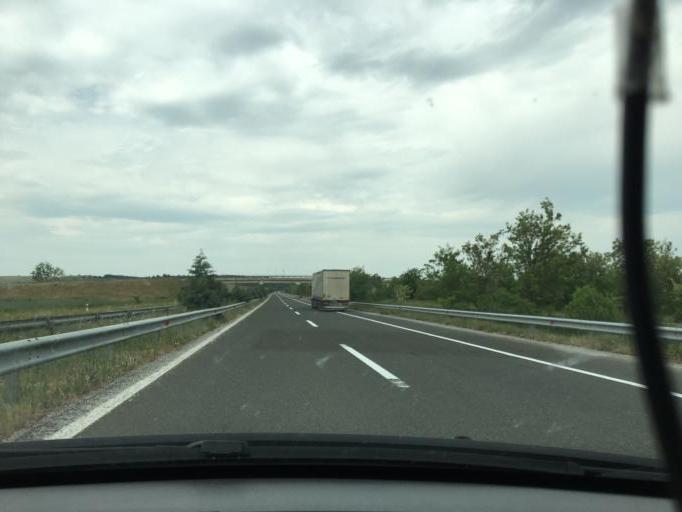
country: MK
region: Negotino
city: Negotino
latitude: 41.5236
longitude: 22.0675
